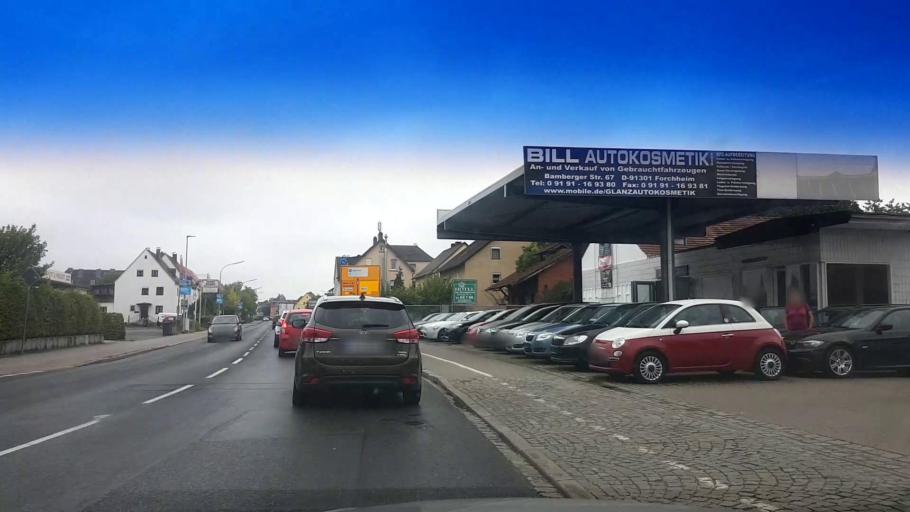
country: DE
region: Bavaria
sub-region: Upper Franconia
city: Forchheim
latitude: 49.7279
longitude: 11.0577
